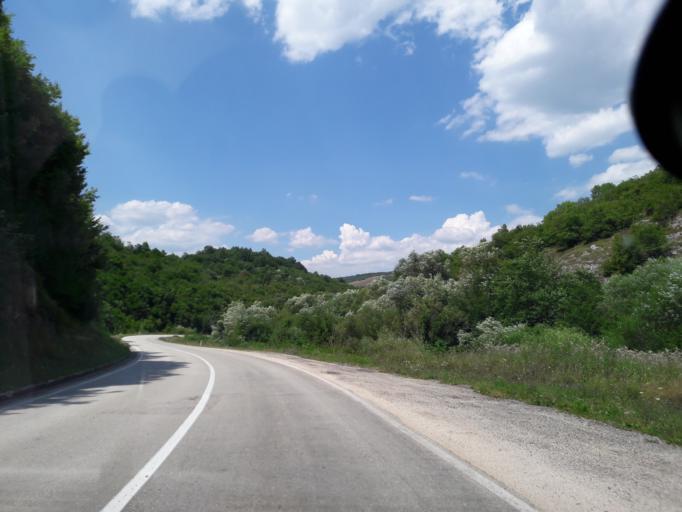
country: BA
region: Republika Srpska
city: Mrkonjic Grad
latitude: 44.4464
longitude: 17.1640
